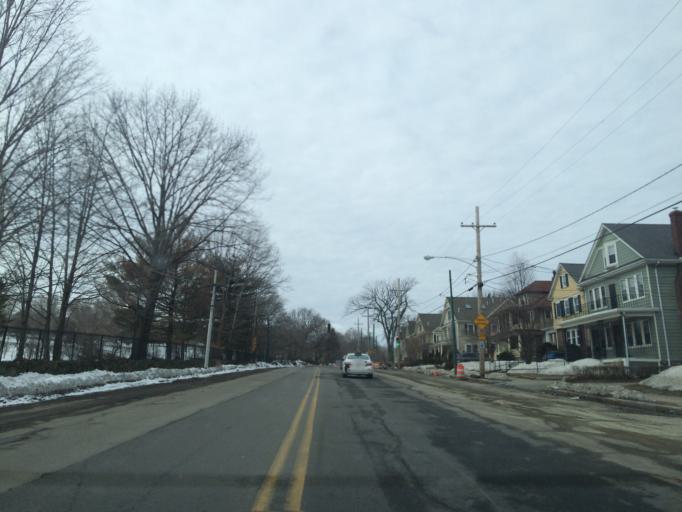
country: US
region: Massachusetts
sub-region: Middlesex County
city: Watertown
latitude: 42.3774
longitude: -71.1676
